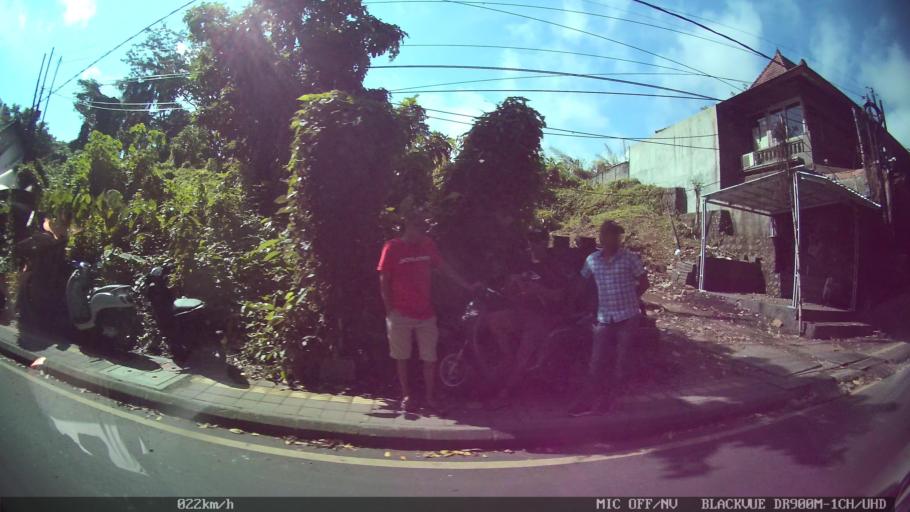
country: ID
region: Bali
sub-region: Kabupaten Gianyar
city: Ubud
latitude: -8.5183
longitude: 115.2615
